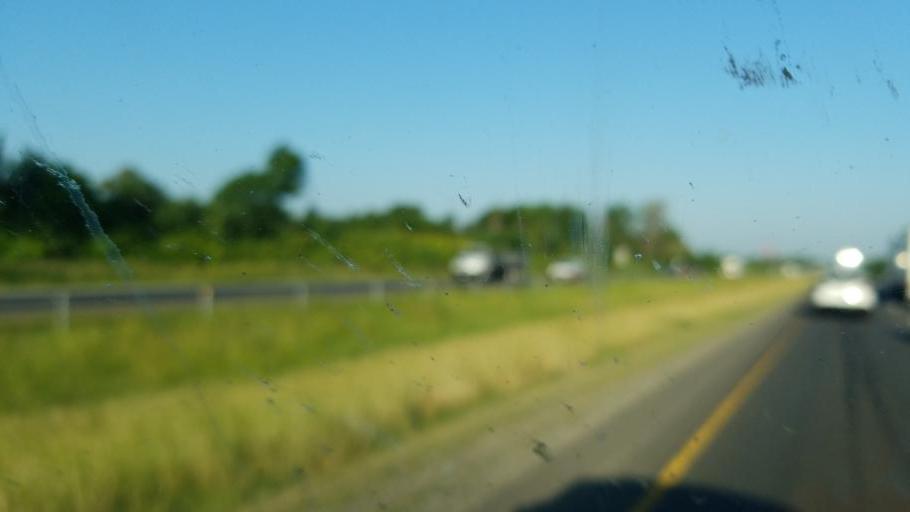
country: US
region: Illinois
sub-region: Will County
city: Ingalls Park
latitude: 41.5135
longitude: -88.0292
